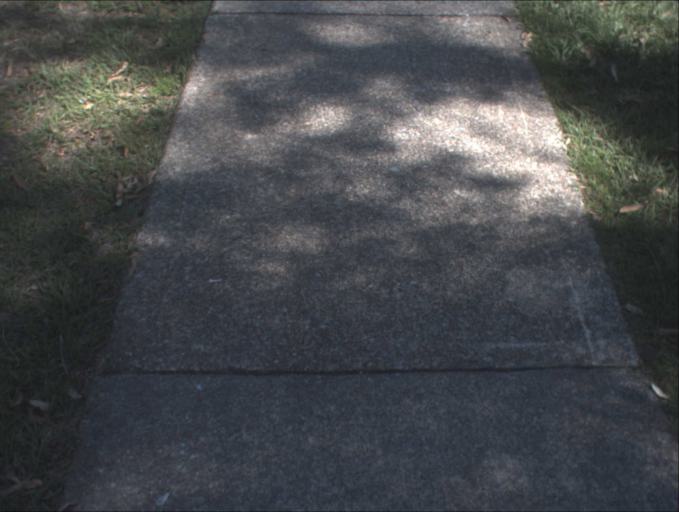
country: AU
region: Queensland
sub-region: Logan
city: Waterford West
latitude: -27.6892
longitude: 153.1535
